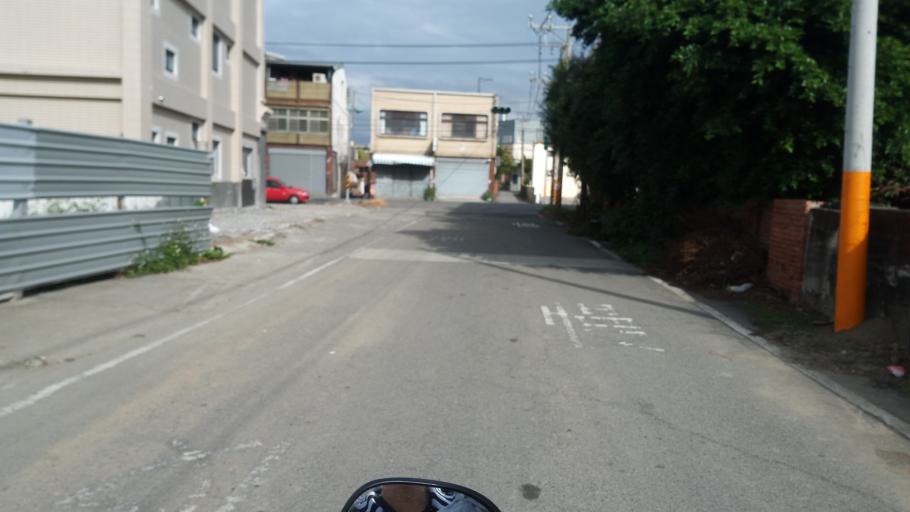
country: TW
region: Taiwan
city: Fengyuan
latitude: 24.4341
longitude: 120.6594
